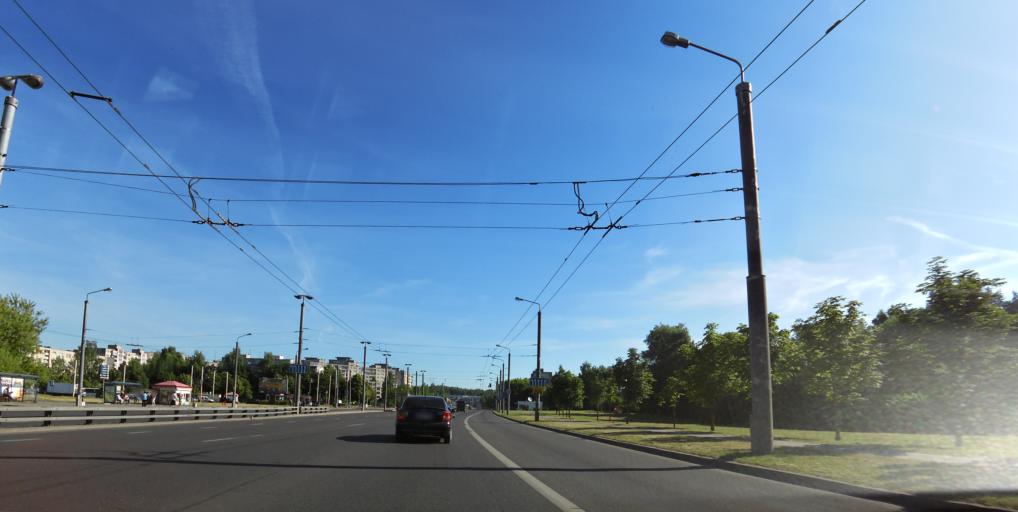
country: LT
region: Vilnius County
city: Justiniskes
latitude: 54.7020
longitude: 25.2239
